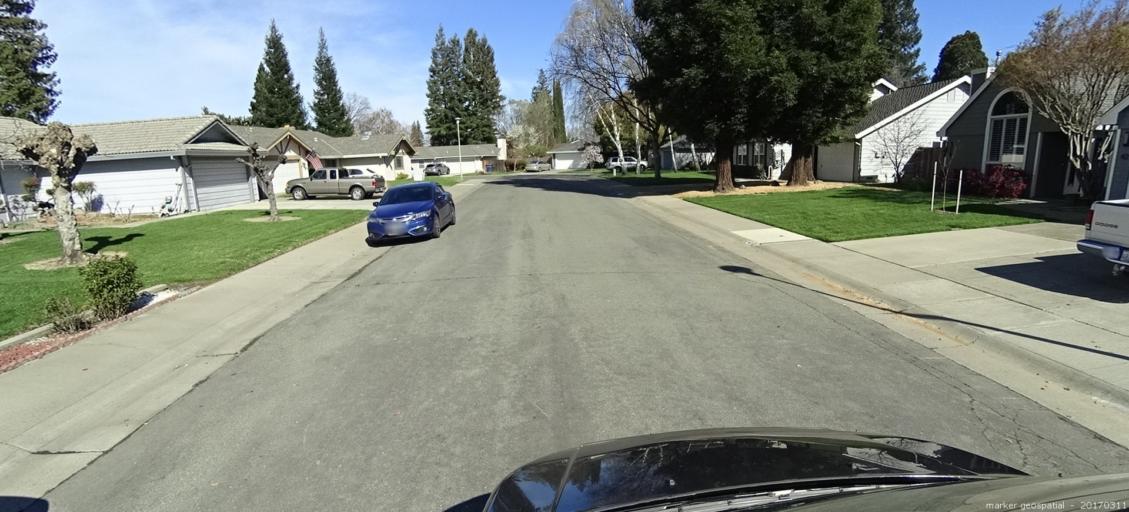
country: US
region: California
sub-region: Sacramento County
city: Parkway
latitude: 38.4918
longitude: -121.5480
